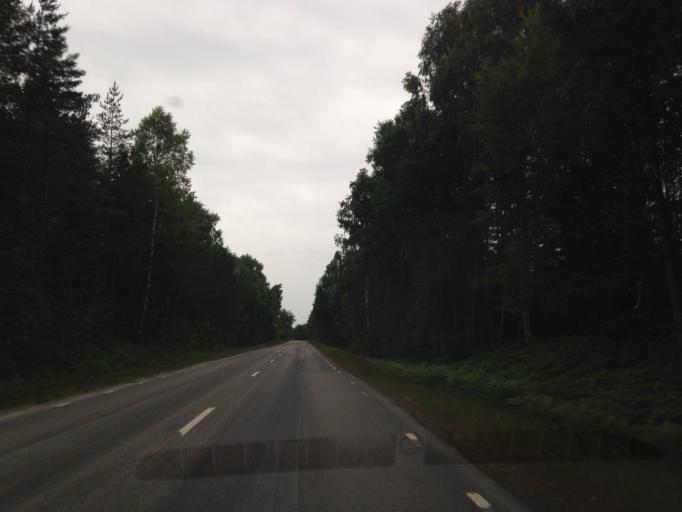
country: SE
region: Vaestra Goetaland
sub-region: Harryda Kommun
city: Hindas
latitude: 57.6738
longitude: 12.3455
